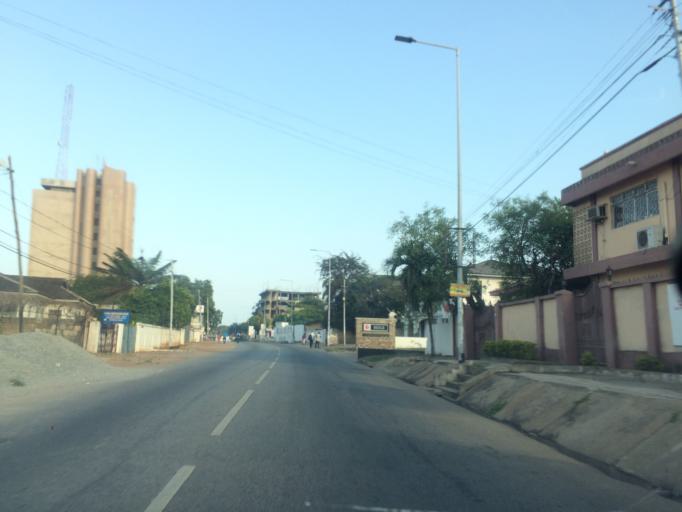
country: GH
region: Greater Accra
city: Accra
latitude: 5.5657
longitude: -0.2091
